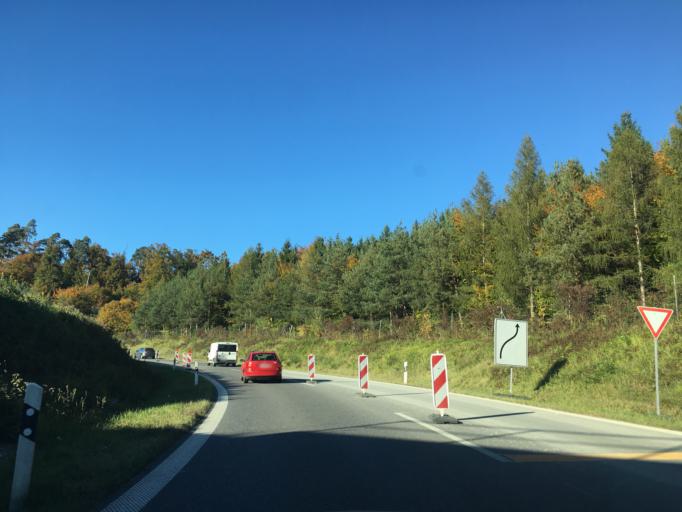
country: DE
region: Baden-Wuerttemberg
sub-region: Freiburg Region
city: Allensbach
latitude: 47.7317
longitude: 9.0302
